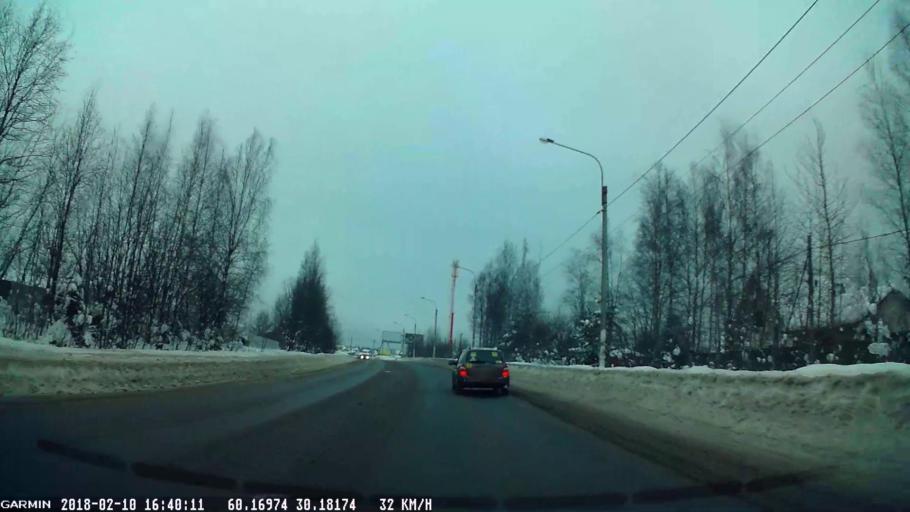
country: RU
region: Leningrad
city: Sertolovo
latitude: 60.1595
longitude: 30.1856
